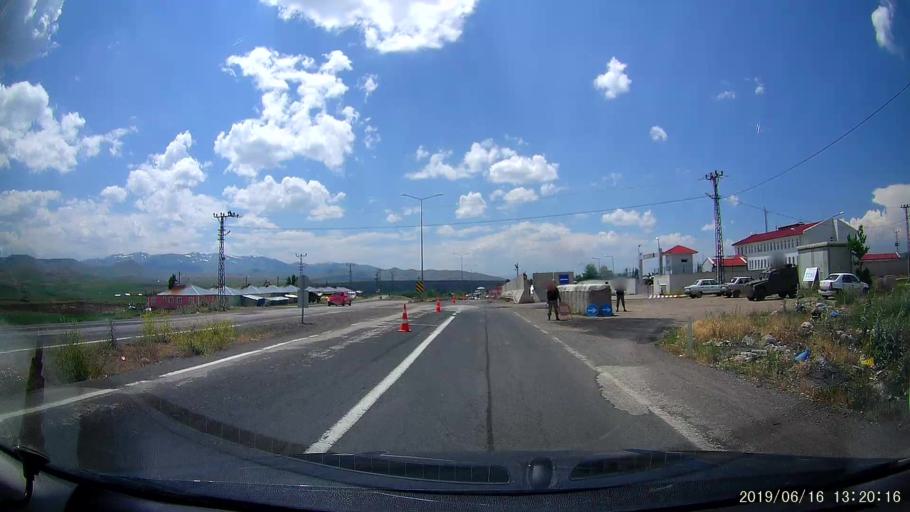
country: TR
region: Agri
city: Taslicay
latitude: 39.6326
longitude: 43.3953
